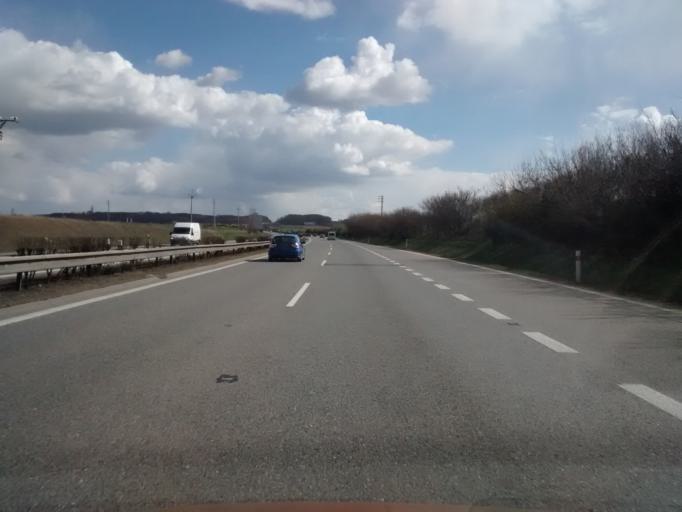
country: CZ
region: Central Bohemia
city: Odolena Voda
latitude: 50.2435
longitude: 14.3785
